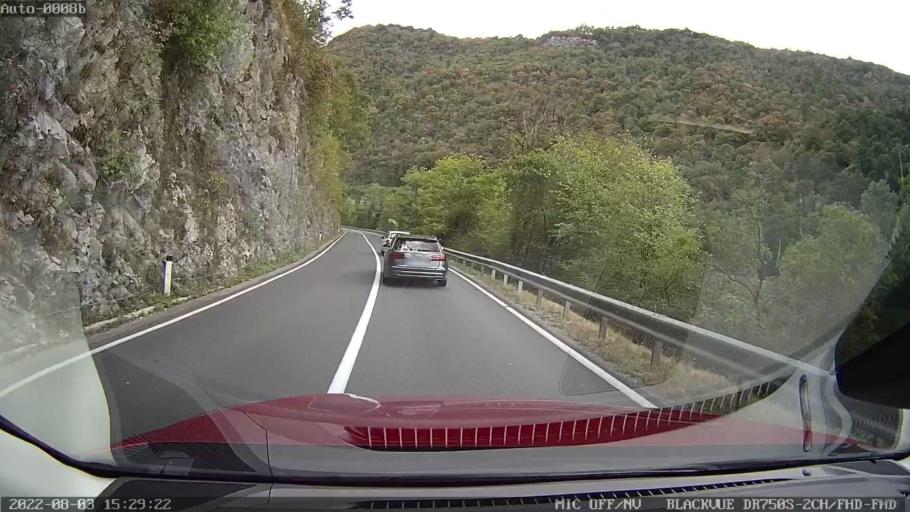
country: SI
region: Kanal
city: Deskle
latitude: 46.0188
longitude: 13.6069
